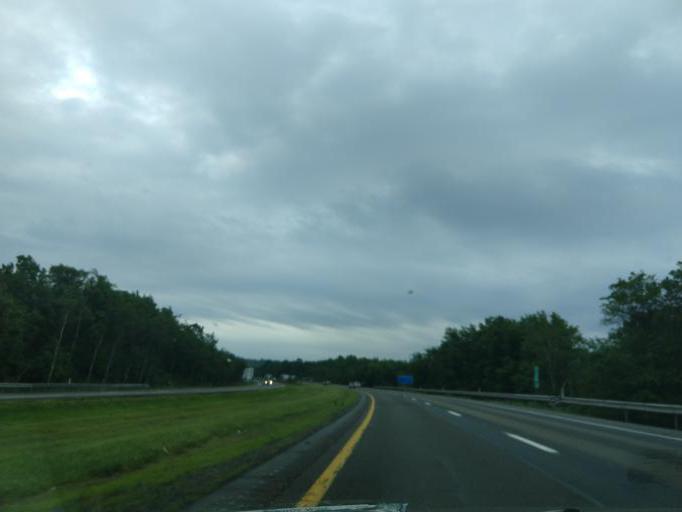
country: US
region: Pennsylvania
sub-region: Schuylkill County
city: McAdoo
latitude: 40.8994
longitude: -76.0302
